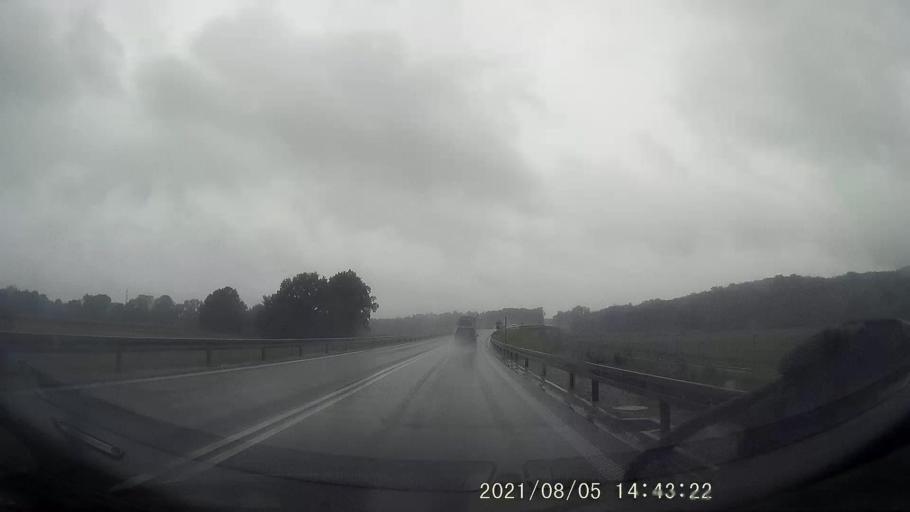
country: PL
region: Opole Voivodeship
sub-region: Powiat nyski
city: Nysa
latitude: 50.4824
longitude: 17.3905
